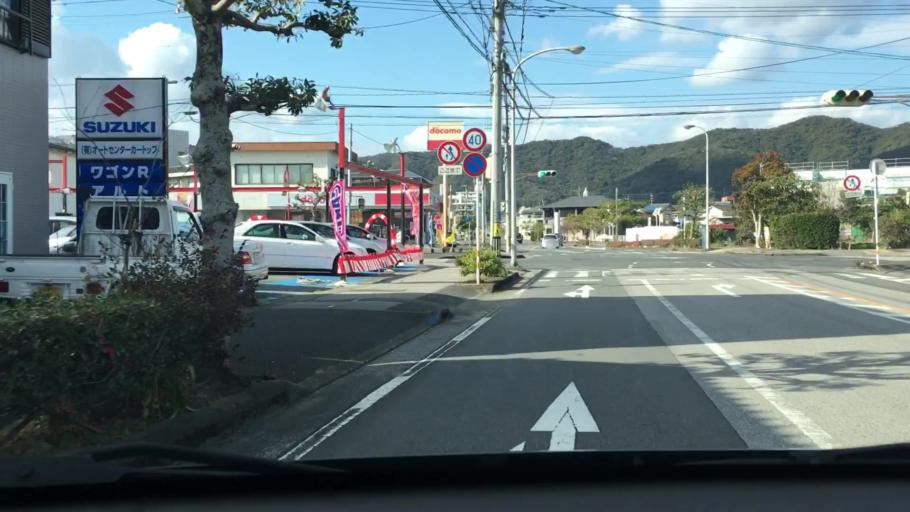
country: JP
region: Oita
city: Saiki
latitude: 32.9582
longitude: 131.9056
